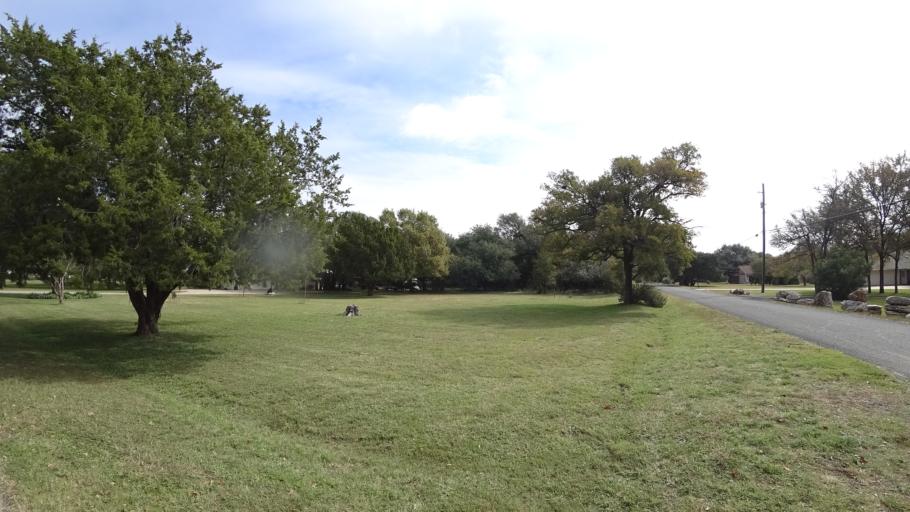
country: US
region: Texas
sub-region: Travis County
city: Wells Branch
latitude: 30.4305
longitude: -97.7067
